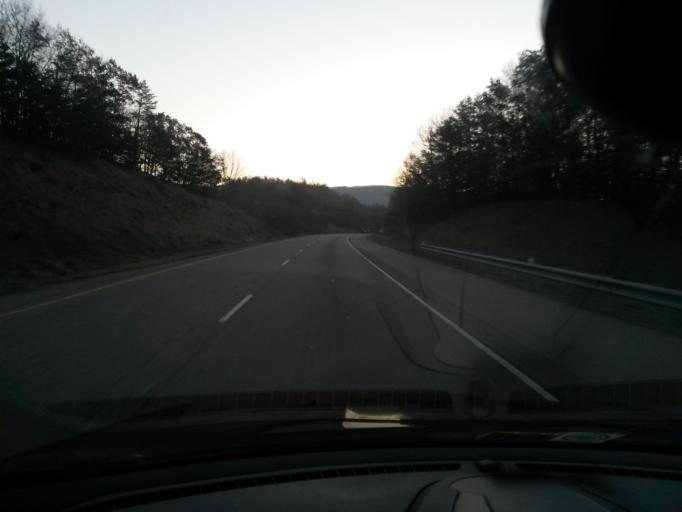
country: US
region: Virginia
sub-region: Alleghany County
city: Clifton Forge
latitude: 37.8312
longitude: -79.7608
